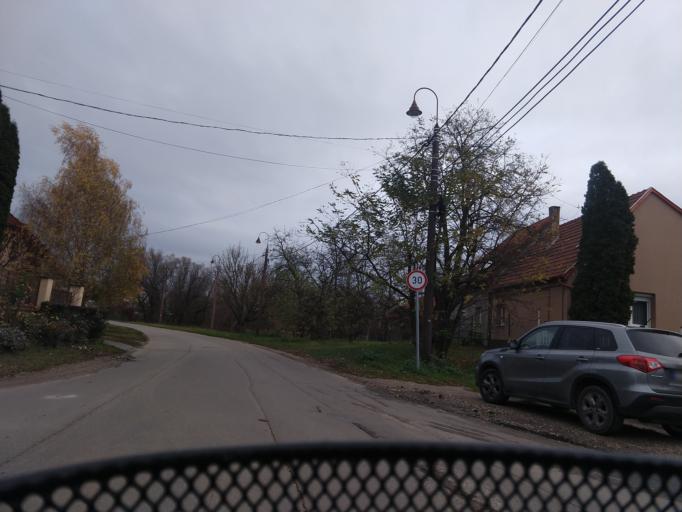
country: HU
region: Pest
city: Veresegyhaz
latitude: 47.6606
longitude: 19.2839
